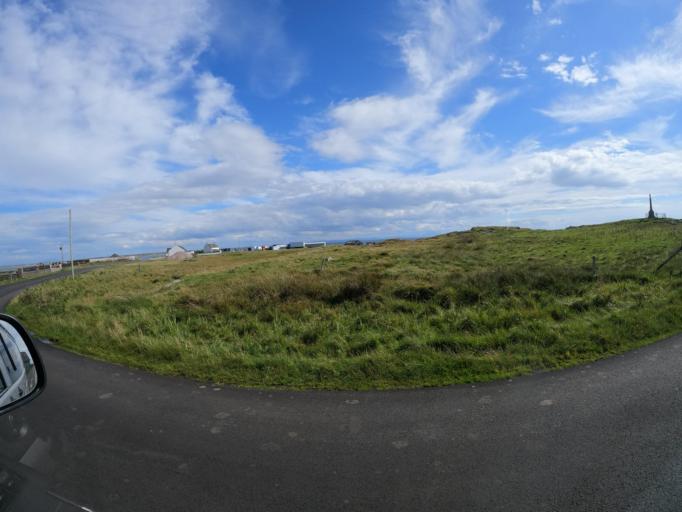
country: GB
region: Scotland
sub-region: Eilean Siar
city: Barra
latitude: 56.5070
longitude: -6.8019
